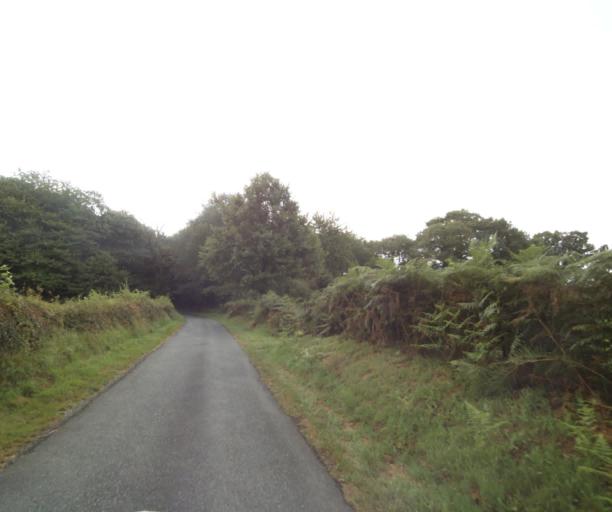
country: FR
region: Limousin
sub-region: Departement de la Correze
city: Sainte-Fortunade
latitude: 45.1921
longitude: 1.8049
